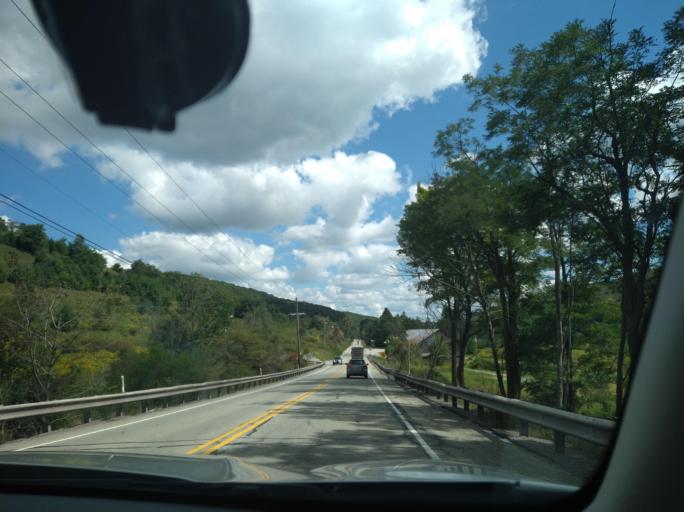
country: US
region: Pennsylvania
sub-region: Westmoreland County
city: Ligonier
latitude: 40.0666
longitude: -79.2485
